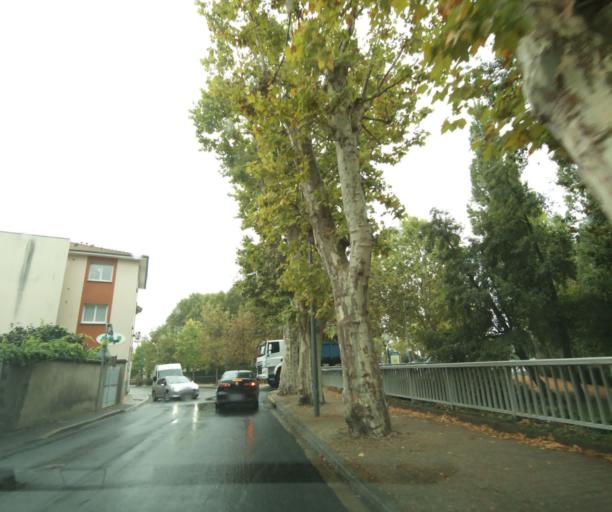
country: FR
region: Auvergne
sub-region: Departement du Puy-de-Dome
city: Cebazat
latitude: 45.8307
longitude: 3.0984
